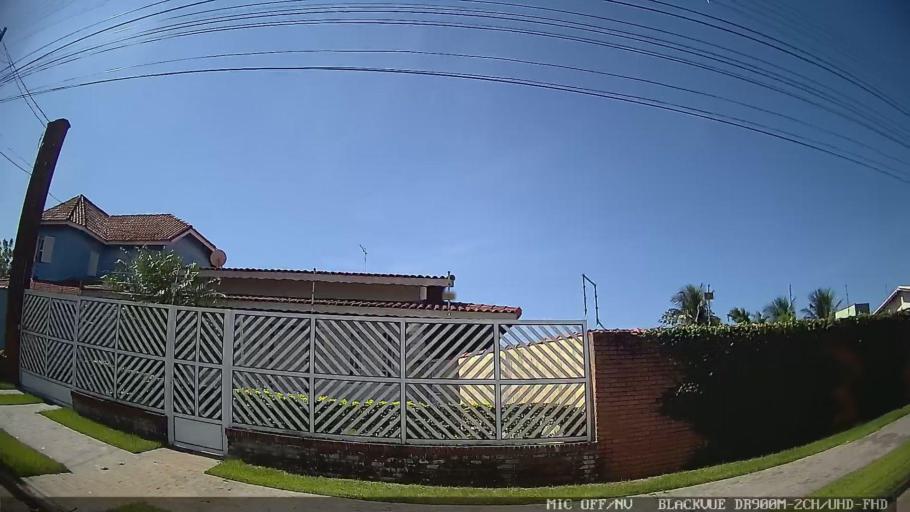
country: BR
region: Sao Paulo
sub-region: Peruibe
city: Peruibe
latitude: -24.2949
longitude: -46.9705
